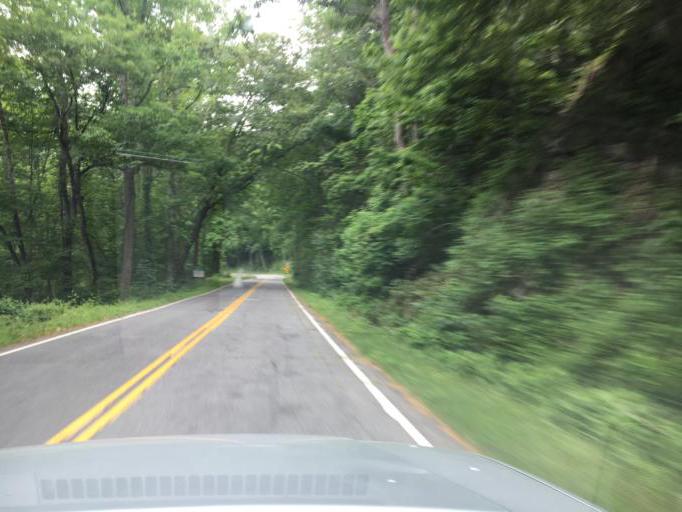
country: US
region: South Carolina
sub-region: Greenville County
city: Tigerville
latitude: 35.1648
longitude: -82.4097
